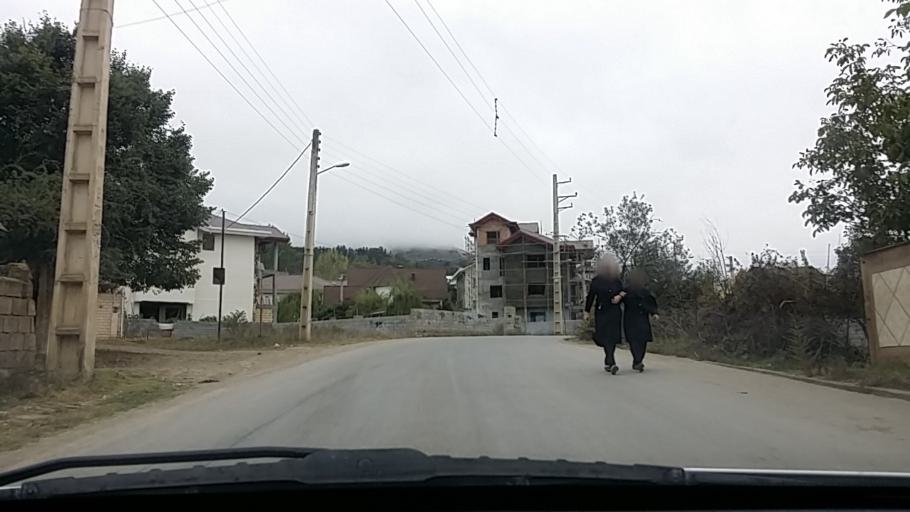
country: IR
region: Mazandaran
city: `Abbasabad
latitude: 36.5000
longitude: 51.1574
